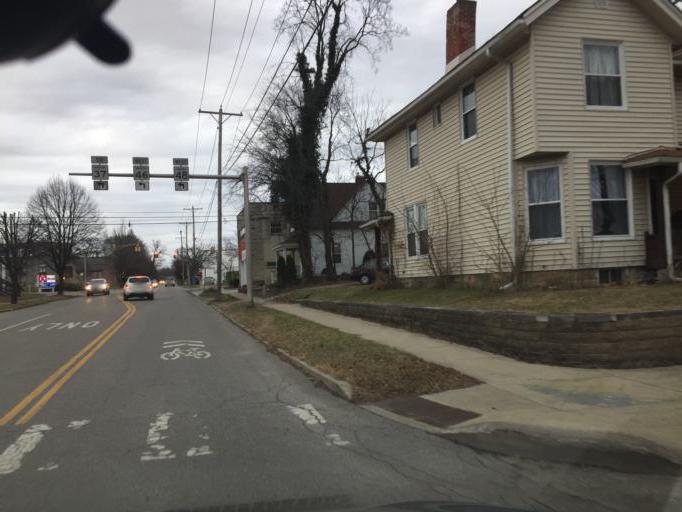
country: US
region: Indiana
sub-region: Monroe County
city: Bloomington
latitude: 39.1655
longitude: -86.5387
